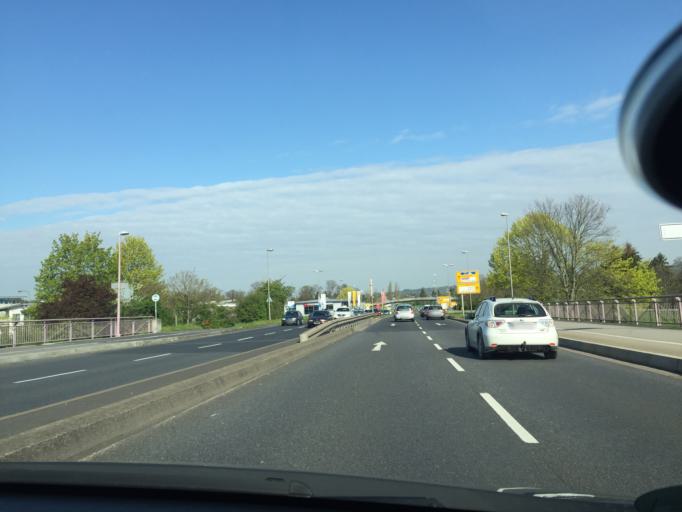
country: DE
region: Bavaria
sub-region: Regierungsbezirk Unterfranken
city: Aschaffenburg
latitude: 49.9678
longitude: 9.1359
